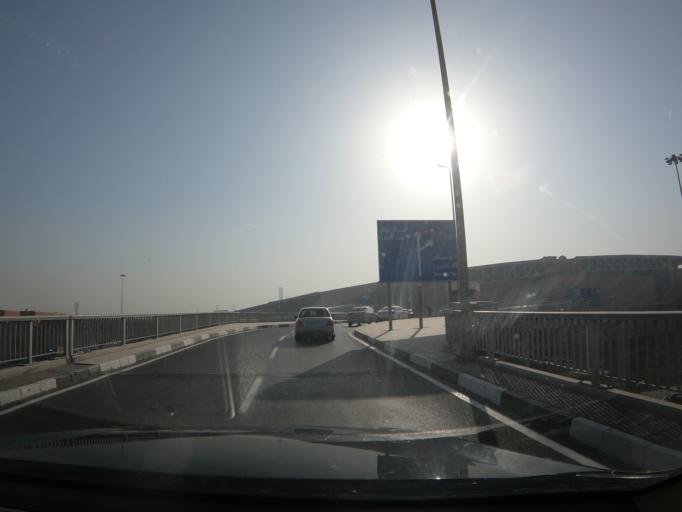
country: EG
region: Muhafazat al Qalyubiyah
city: Al Khankah
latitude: 30.1119
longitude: 31.3946
